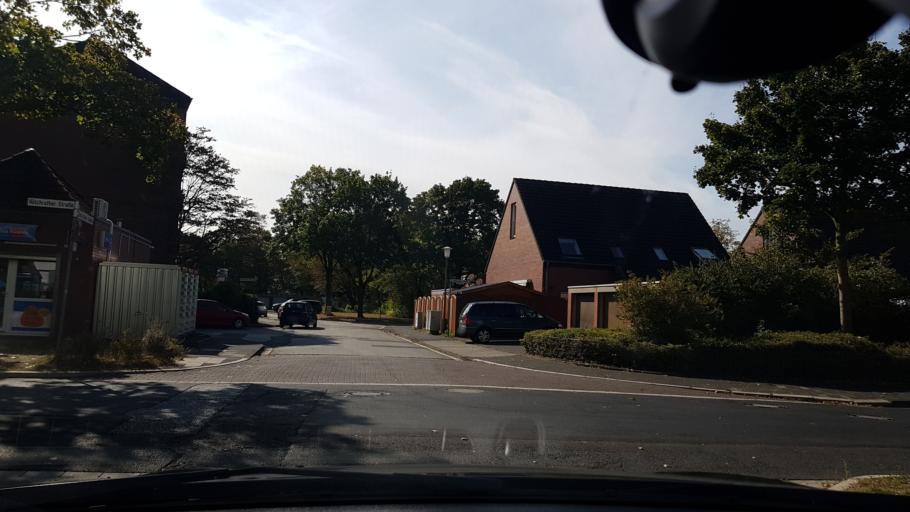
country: DE
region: North Rhine-Westphalia
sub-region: Regierungsbezirk Dusseldorf
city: Neuss
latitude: 51.1524
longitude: 6.6959
